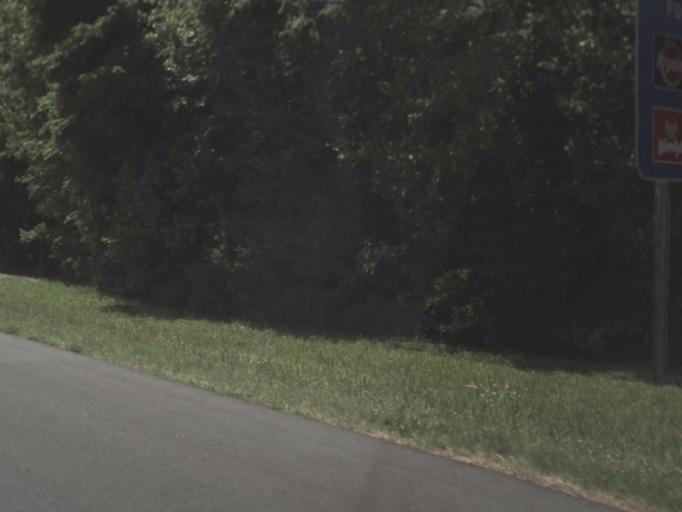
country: US
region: Florida
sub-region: Nassau County
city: Yulee
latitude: 30.6275
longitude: -81.6530
